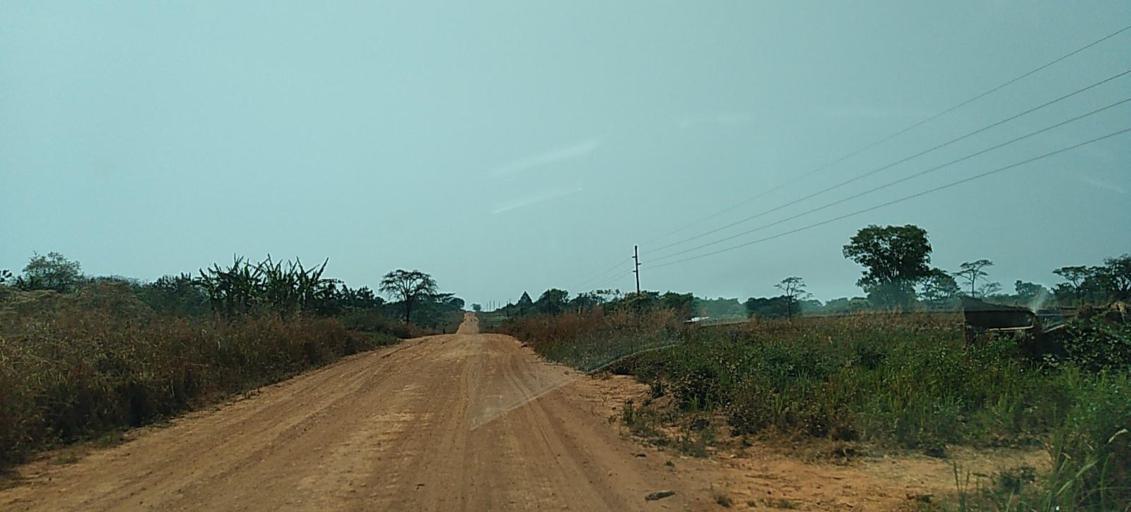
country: ZM
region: North-Western
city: Kansanshi
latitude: -12.0060
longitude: 26.5702
